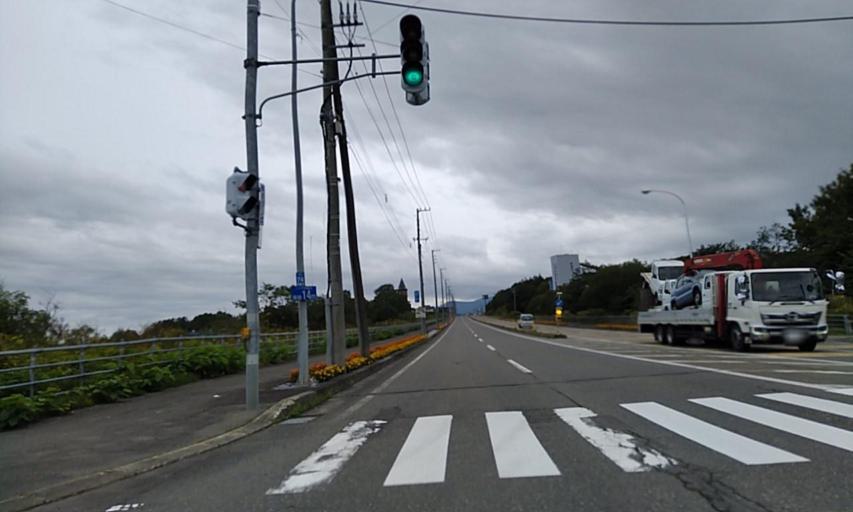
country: JP
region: Hokkaido
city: Obihiro
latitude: 42.3113
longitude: 143.3212
